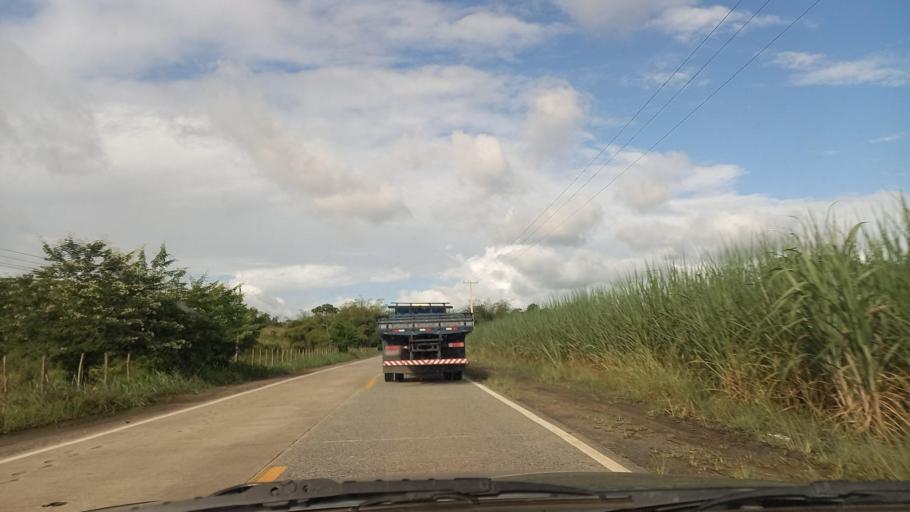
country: BR
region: Pernambuco
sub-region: Palmares
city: Palmares
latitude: -8.6915
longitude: -35.6295
